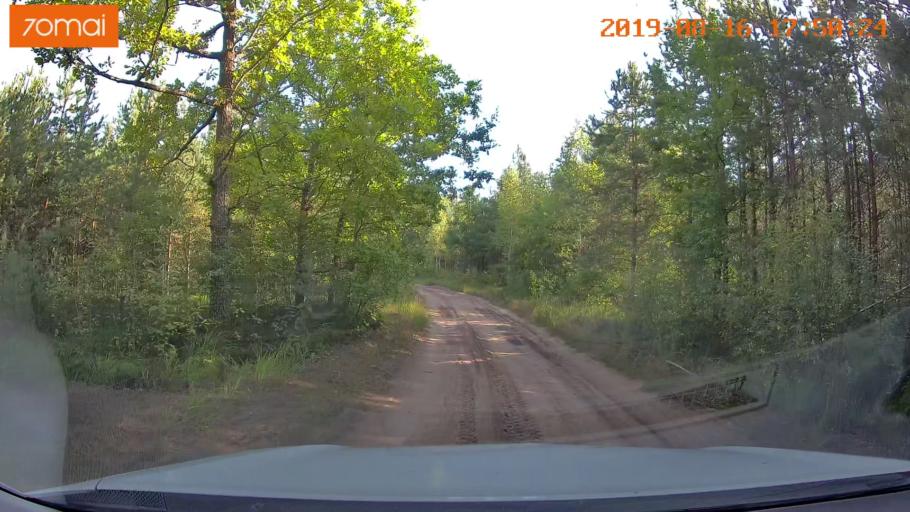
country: BY
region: Mogilev
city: Asipovichy
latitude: 53.2269
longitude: 28.6590
